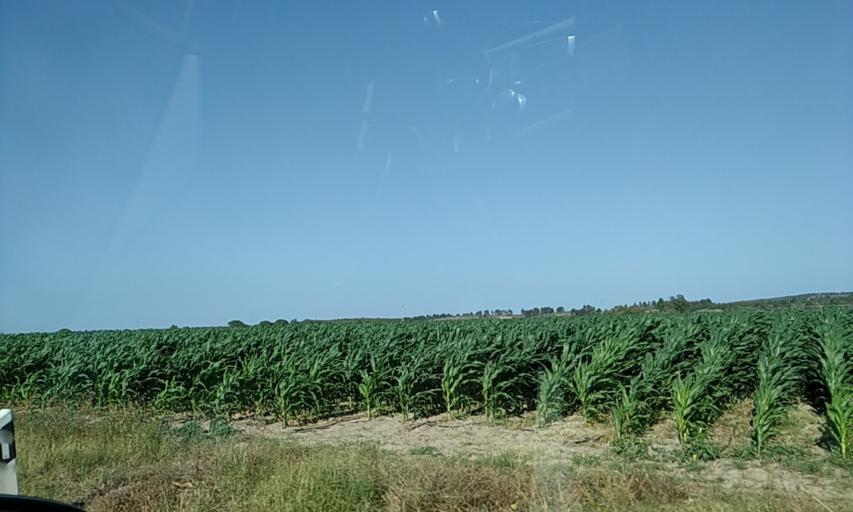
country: PT
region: Santarem
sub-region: Almeirim
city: Almeirim
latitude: 39.1582
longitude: -8.6203
